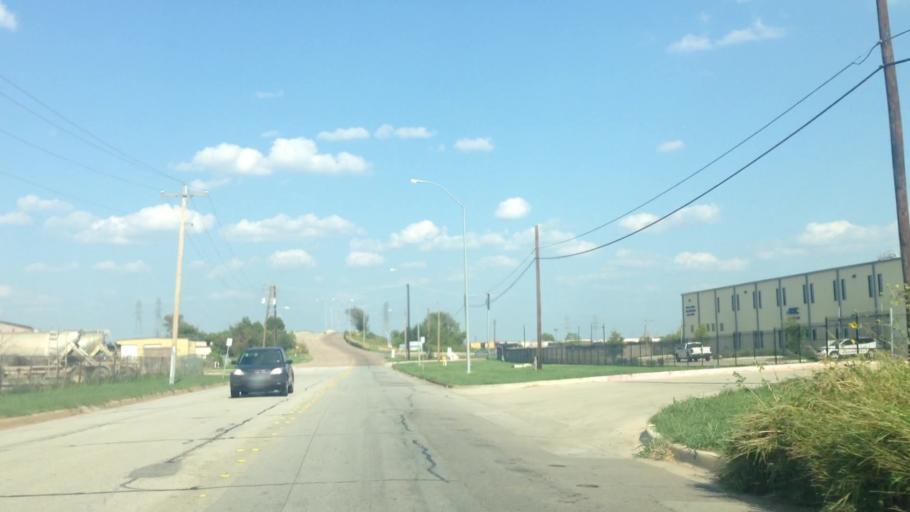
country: US
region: Texas
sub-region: Tarrant County
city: Blue Mound
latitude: 32.8248
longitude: -97.3377
